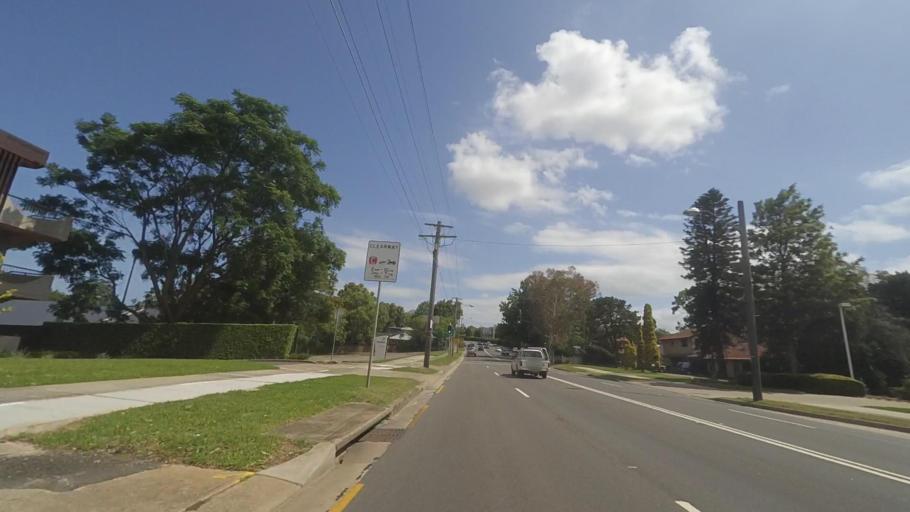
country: AU
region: New South Wales
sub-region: The Hills Shire
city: West Pennant
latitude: -33.7639
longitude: 151.0477
